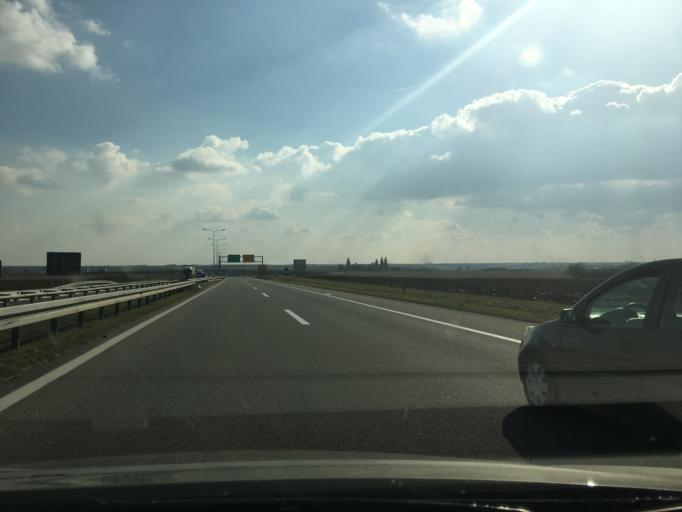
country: RS
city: Beska
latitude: 45.1424
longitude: 20.0851
